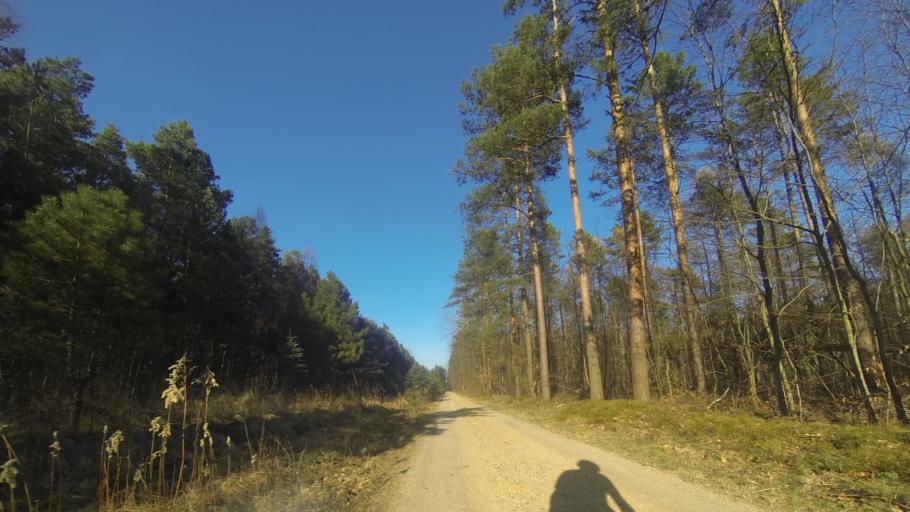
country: DE
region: Saxony
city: Tauscha
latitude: 51.2496
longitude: 13.8374
